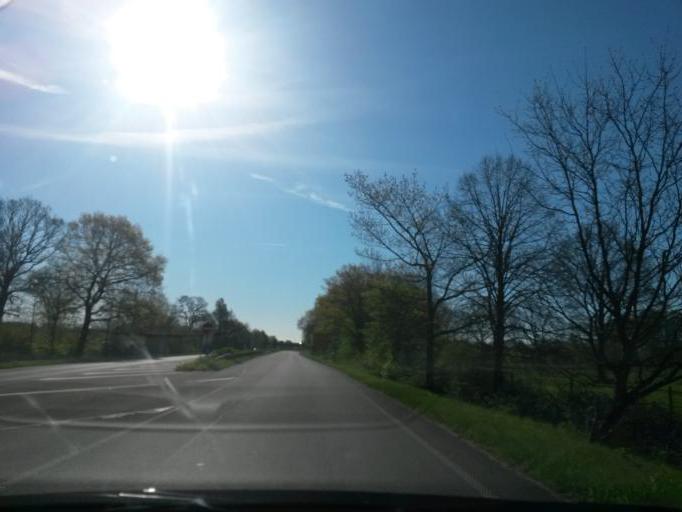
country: DE
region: Schleswig-Holstein
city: Rellingen
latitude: 53.6105
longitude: 9.8073
